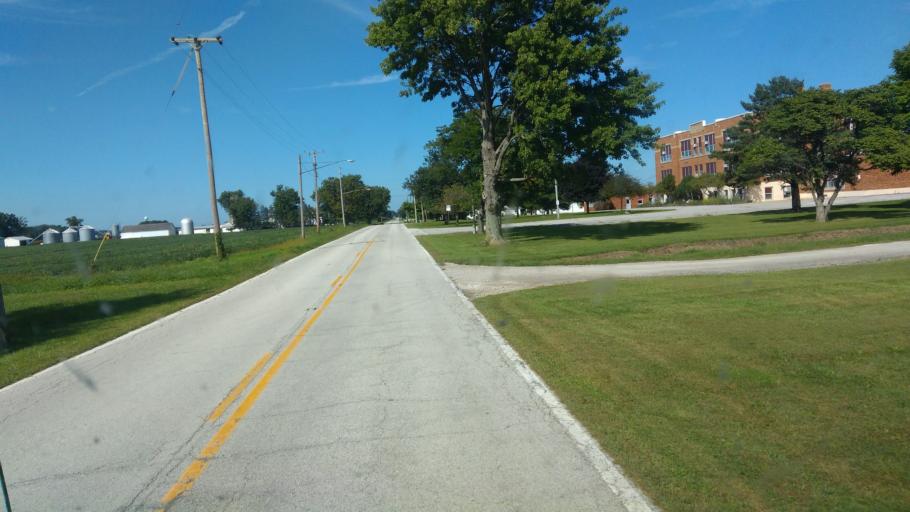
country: US
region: Ohio
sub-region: Sandusky County
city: Clyde
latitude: 41.3908
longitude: -82.8921
